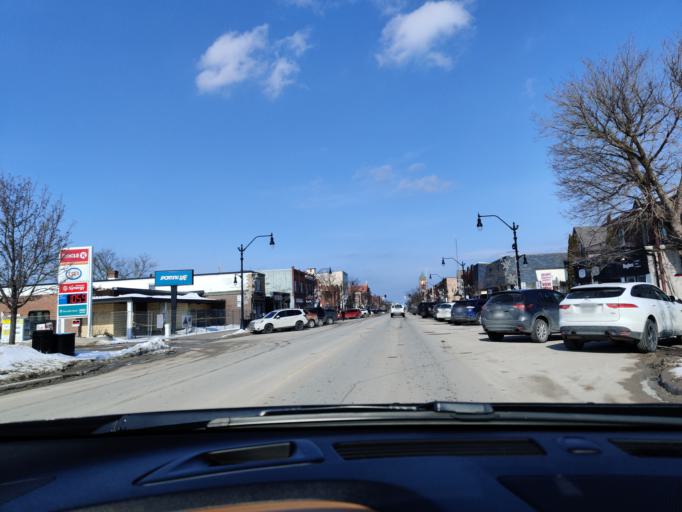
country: CA
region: Ontario
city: Collingwood
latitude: 44.4970
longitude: -80.2162
